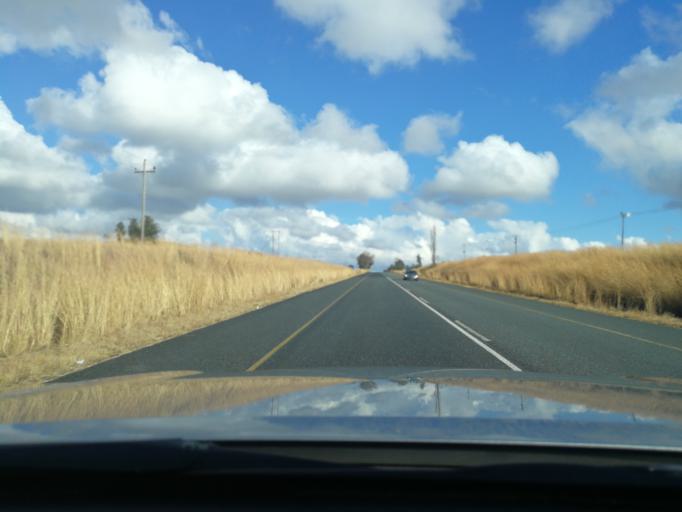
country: ZA
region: Orange Free State
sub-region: Thabo Mofutsanyana District Municipality
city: Reitz
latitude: -27.9956
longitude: 28.3757
